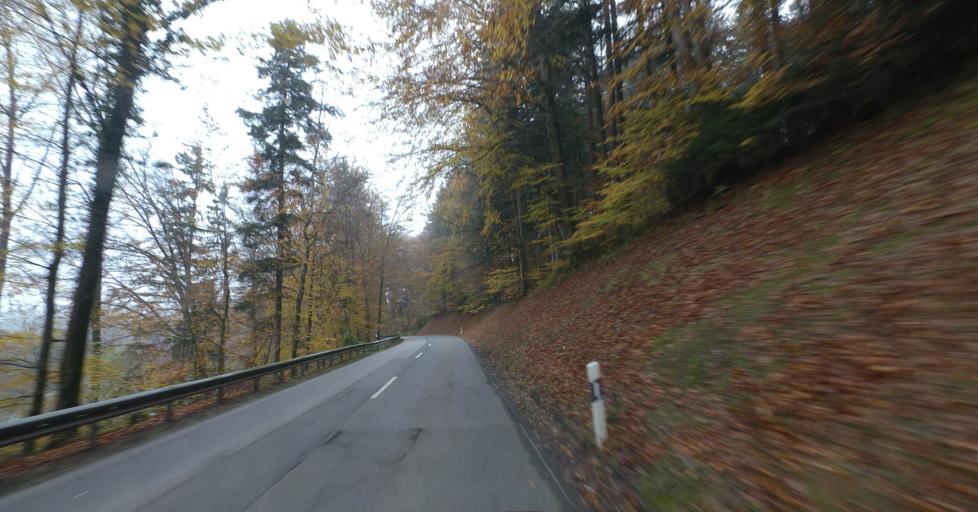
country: DE
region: Bavaria
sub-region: Upper Bavaria
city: Seeon-Seebruck
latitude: 47.9619
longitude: 12.5109
